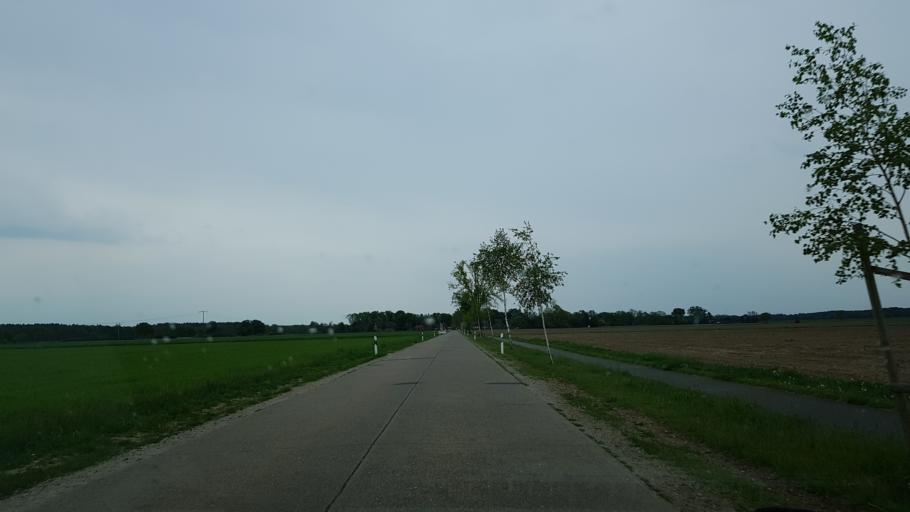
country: DE
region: Lower Saxony
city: Gartow
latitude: 53.0491
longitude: 11.4386
